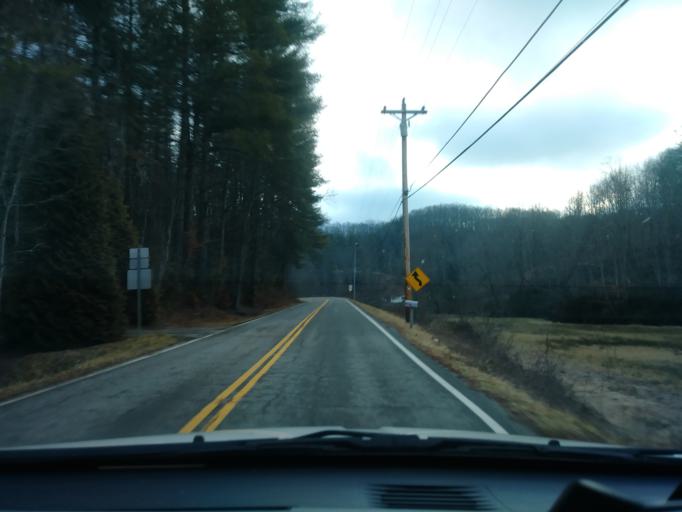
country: US
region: Tennessee
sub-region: Unicoi County
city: Unicoi
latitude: 36.2107
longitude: -82.2238
